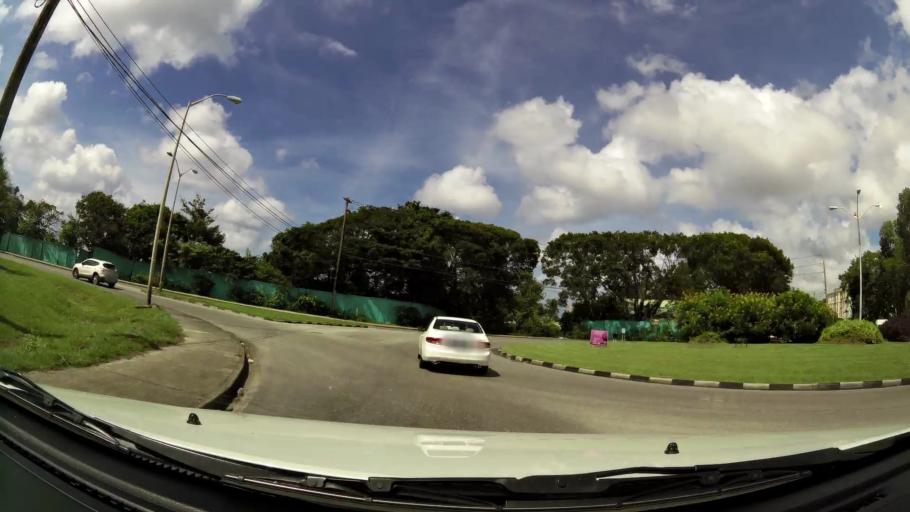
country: BB
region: Saint Michael
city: Bridgetown
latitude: 13.1316
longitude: -59.6331
